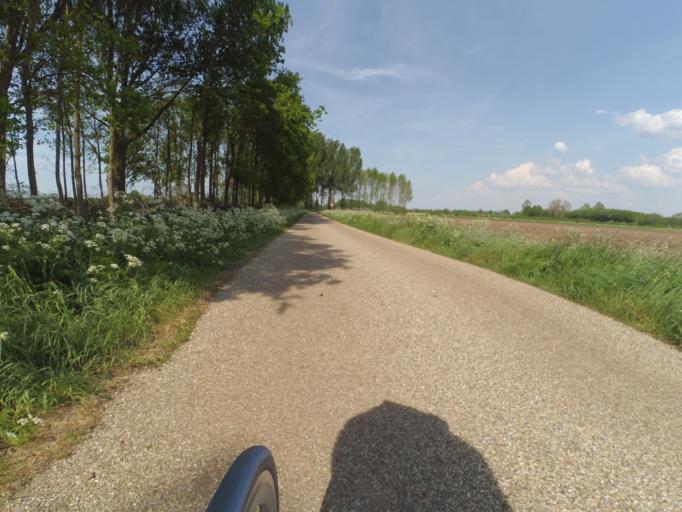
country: NL
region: Overijssel
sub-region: Gemeente Tubbergen
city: Tubbergen
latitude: 52.3554
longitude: 6.7849
